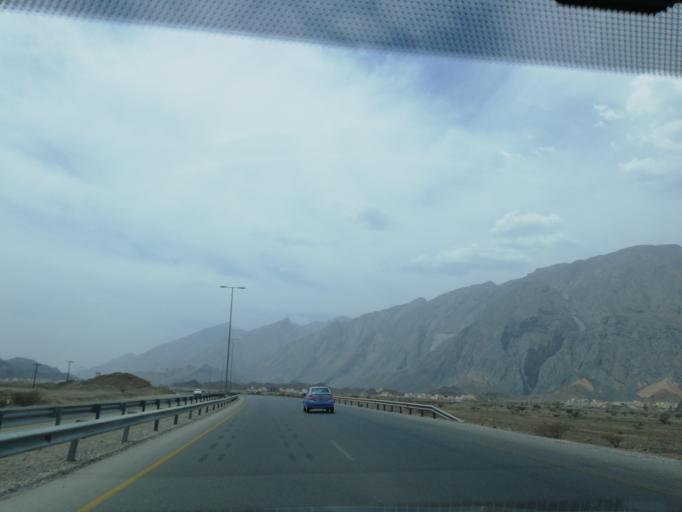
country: OM
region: Muhafazat ad Dakhiliyah
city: Sufalat Sama'il
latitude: 23.2099
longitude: 57.8929
